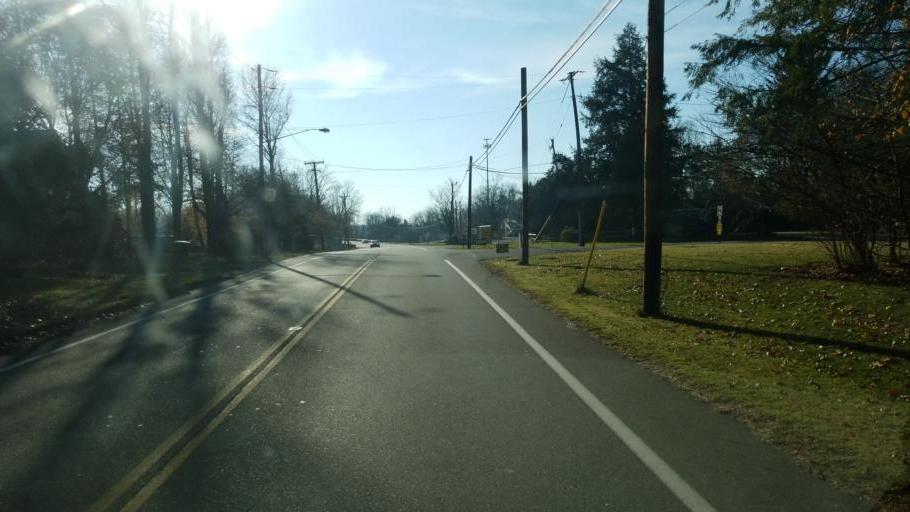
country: US
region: Ohio
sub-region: Portage County
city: Kent
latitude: 41.1901
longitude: -81.3443
